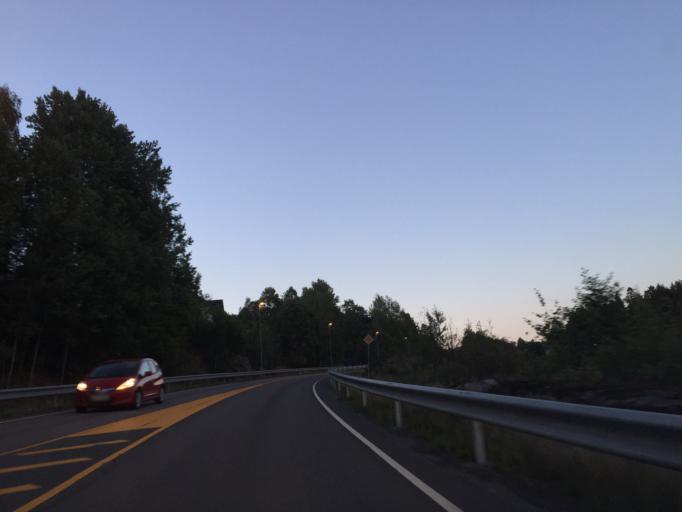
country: NO
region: Ostfold
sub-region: Moss
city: Moss
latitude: 59.5163
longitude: 10.6921
